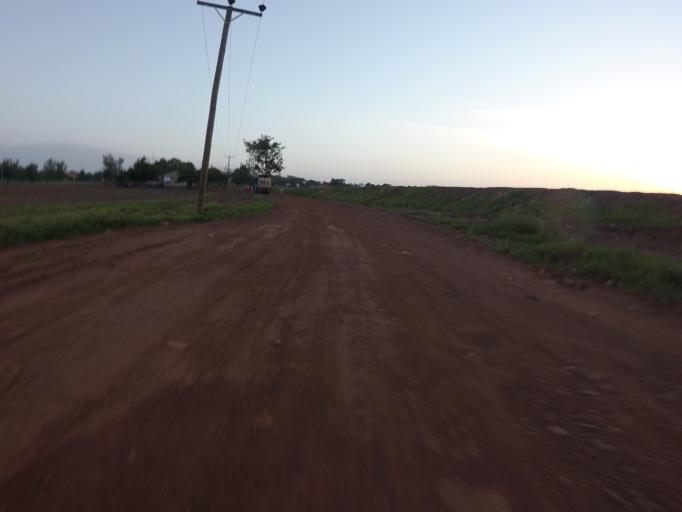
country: GH
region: Northern
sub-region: Yendi
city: Yendi
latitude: 9.9278
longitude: -0.2096
